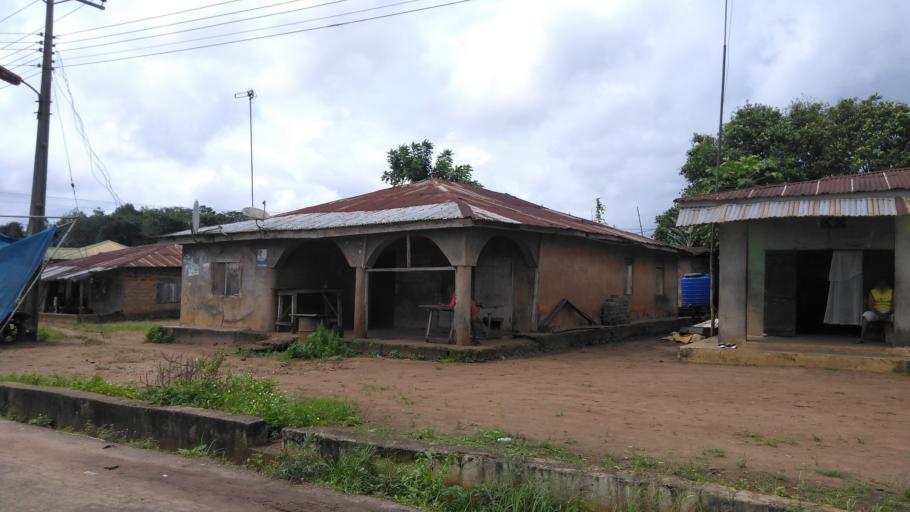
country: NG
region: Ogun
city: Abigi
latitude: 6.6032
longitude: 4.4891
